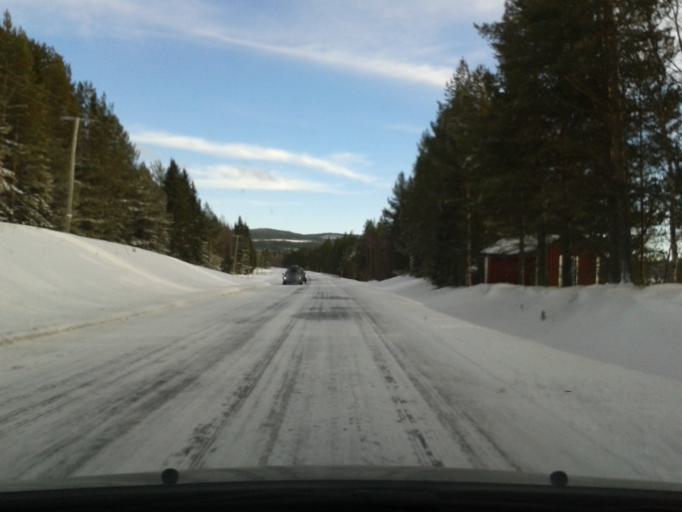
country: SE
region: Vaesterbotten
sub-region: Asele Kommun
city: Asele
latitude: 64.3417
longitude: 17.0172
